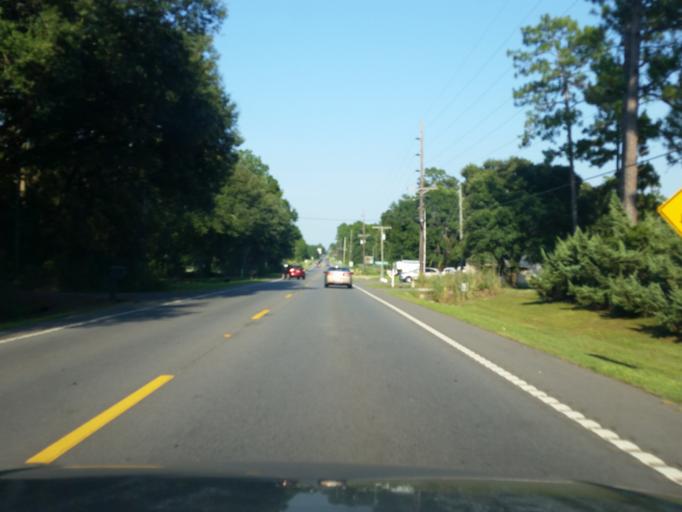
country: US
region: Alabama
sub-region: Baldwin County
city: Elberta
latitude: 30.4068
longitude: -87.6339
